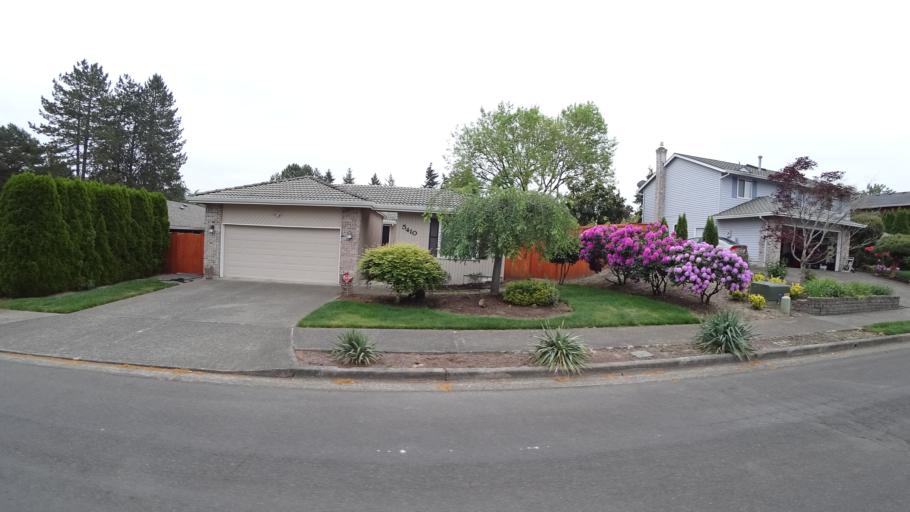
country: US
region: Oregon
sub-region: Washington County
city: Rockcreek
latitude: 45.5589
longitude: -122.8853
